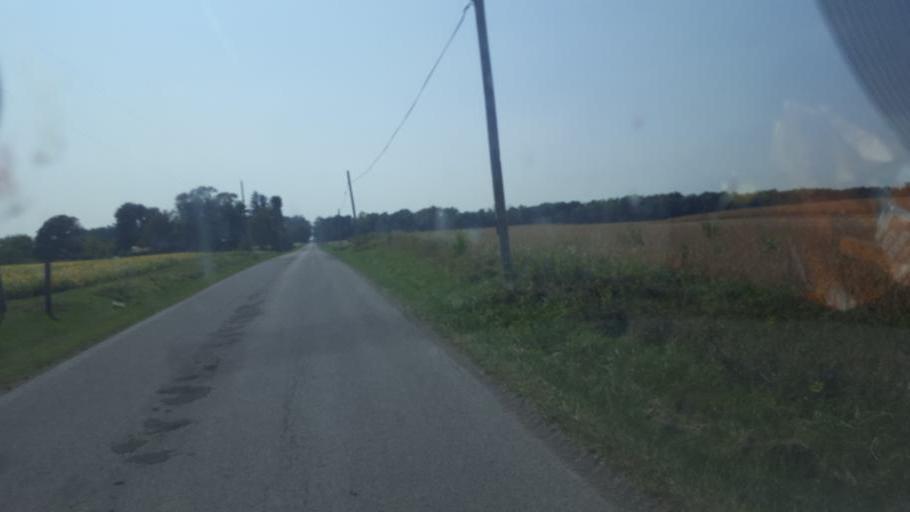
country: US
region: Ohio
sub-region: Morrow County
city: Mount Gilead
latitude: 40.6394
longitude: -82.8416
